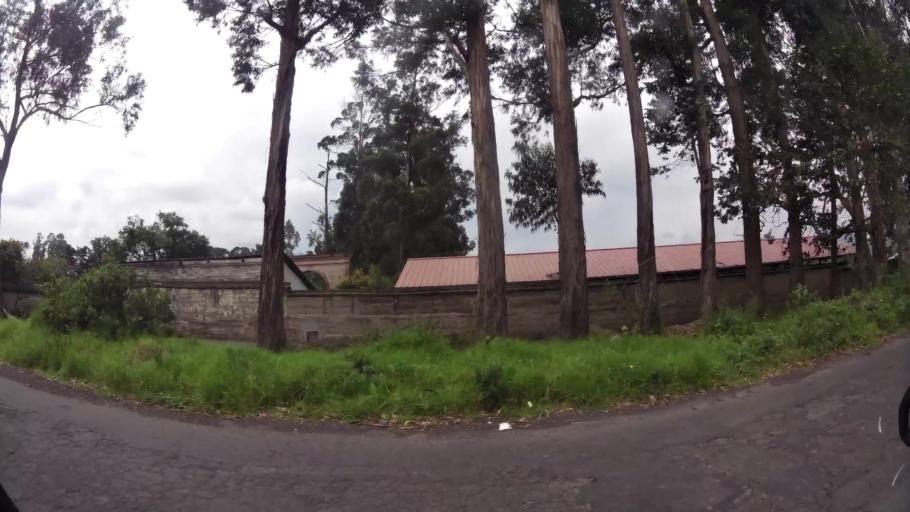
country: EC
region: Pichincha
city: Sangolqui
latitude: -0.3521
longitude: -78.4748
